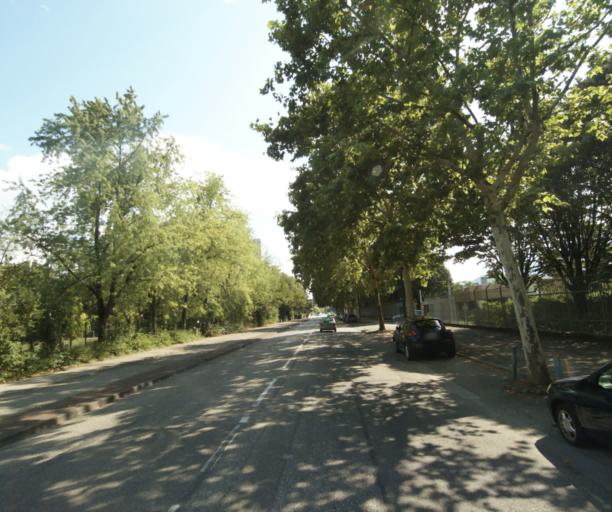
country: FR
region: Rhone-Alpes
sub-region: Departement de l'Isere
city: Seyssinet-Pariset
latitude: 45.1766
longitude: 5.7052
